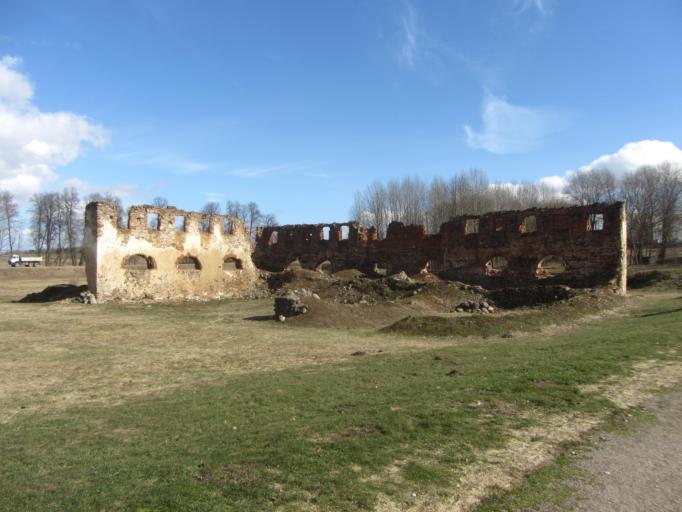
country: LT
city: Salcininkai
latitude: 54.4565
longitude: 25.4744
